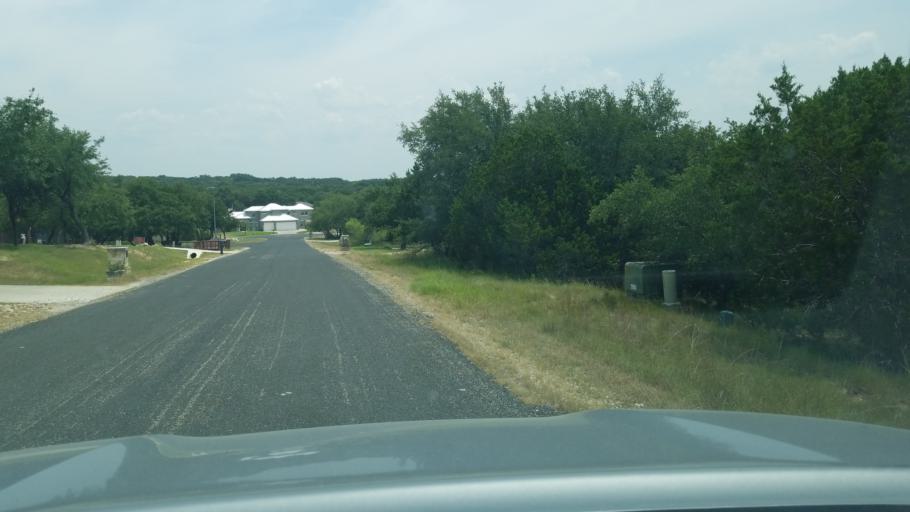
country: US
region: Texas
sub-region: Bexar County
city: Timberwood Park
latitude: 29.6892
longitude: -98.5072
